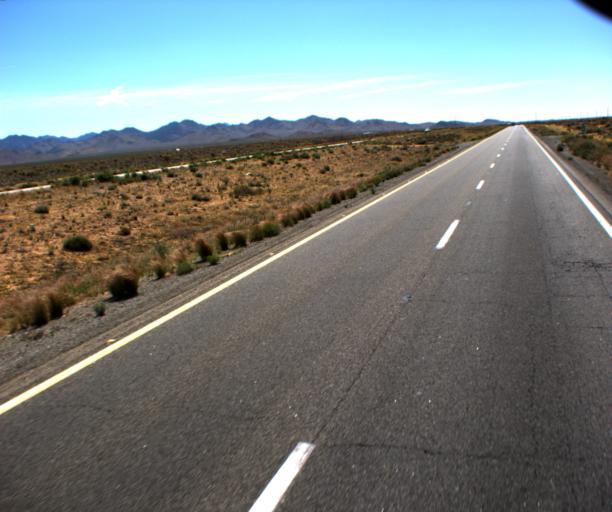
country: US
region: Arizona
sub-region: Mohave County
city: Dolan Springs
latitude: 35.5076
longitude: -114.3374
